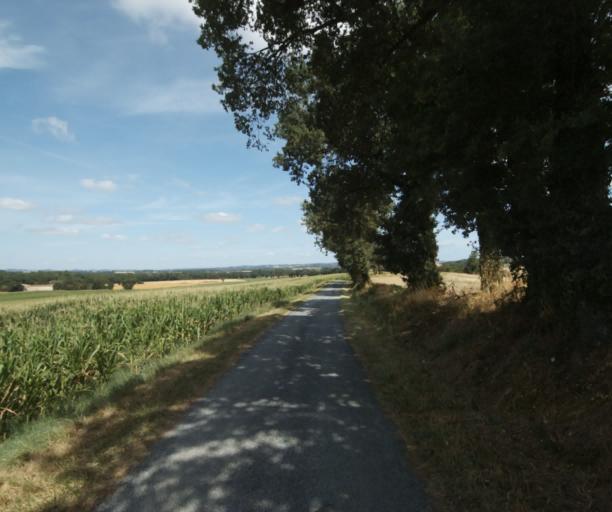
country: FR
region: Midi-Pyrenees
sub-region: Departement du Tarn
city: Dourgne
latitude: 43.4906
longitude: 2.0972
